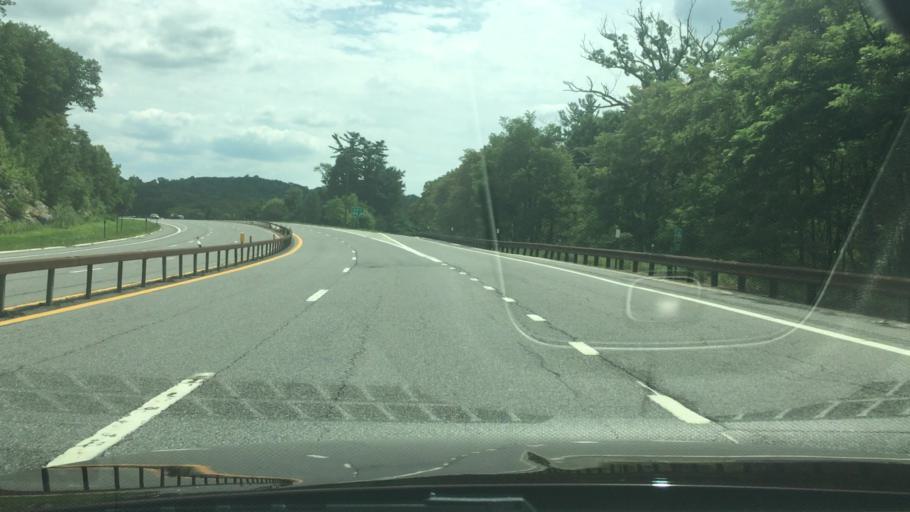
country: US
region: New York
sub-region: Westchester County
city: Shrub Oak
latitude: 41.3362
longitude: -73.8175
